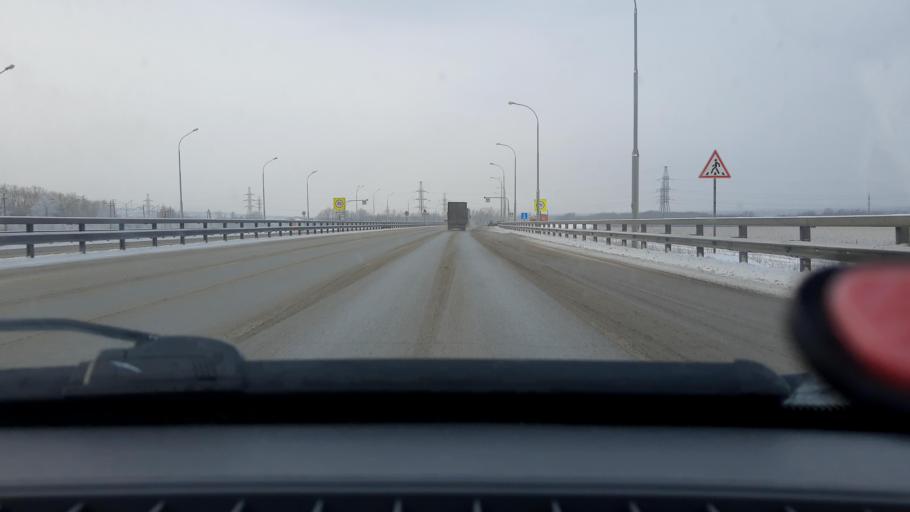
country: RU
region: Bashkortostan
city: Kabakovo
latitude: 54.6531
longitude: 56.1150
